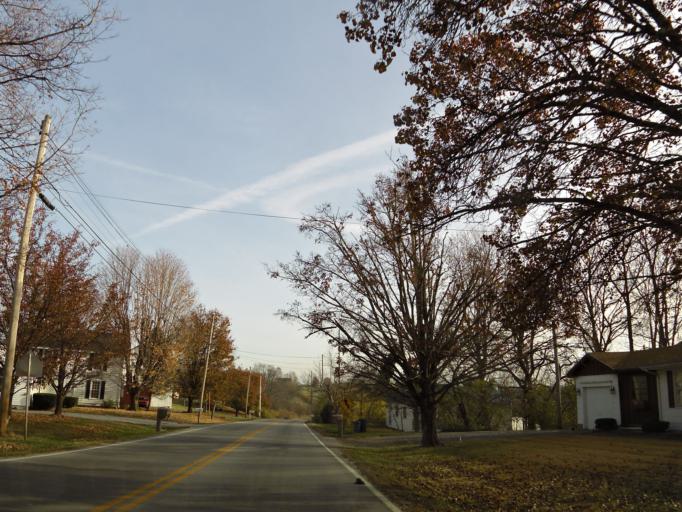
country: US
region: Kentucky
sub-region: Harrison County
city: Cynthiana
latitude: 38.3793
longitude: -84.2932
